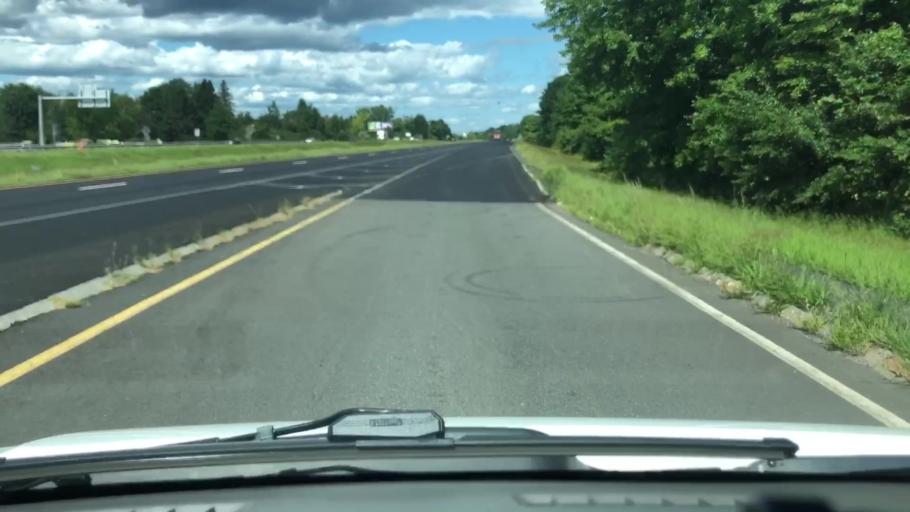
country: US
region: Massachusetts
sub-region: Hampshire County
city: Hatfield
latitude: 42.3631
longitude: -72.6354
